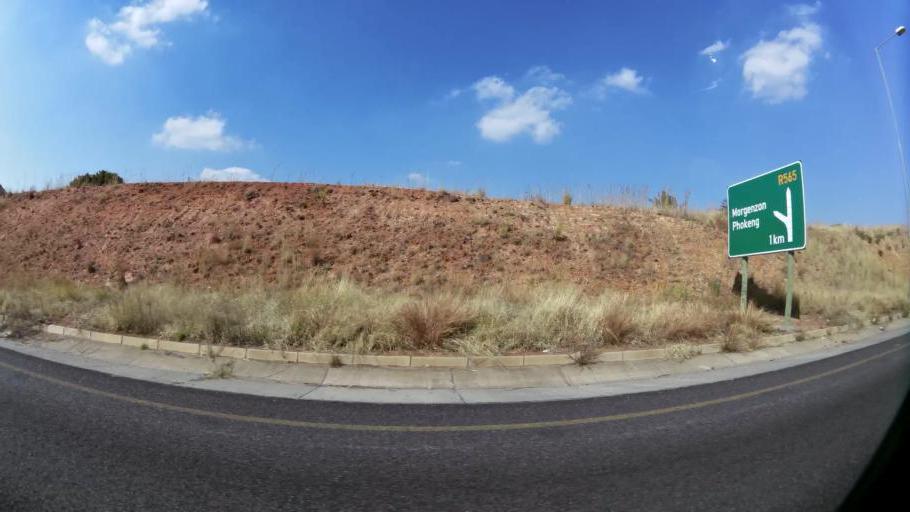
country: ZA
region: North-West
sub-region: Bojanala Platinum District Municipality
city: Rustenburg
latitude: -25.5878
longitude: 27.1281
